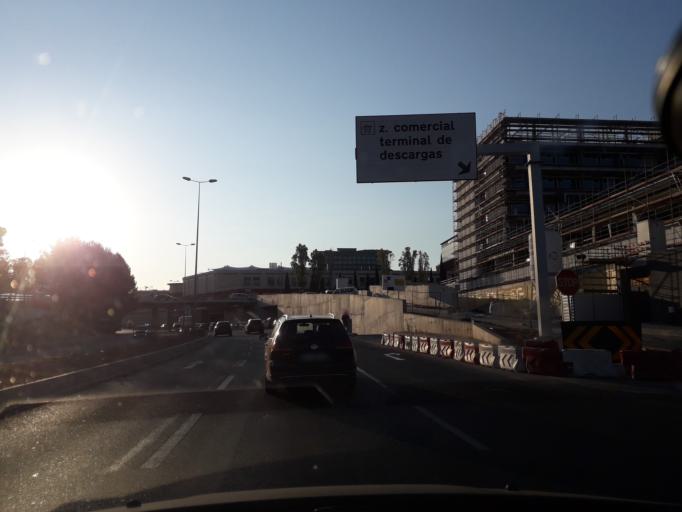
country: PT
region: Lisbon
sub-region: Odivelas
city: Pontinha
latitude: 38.7567
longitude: -9.1917
